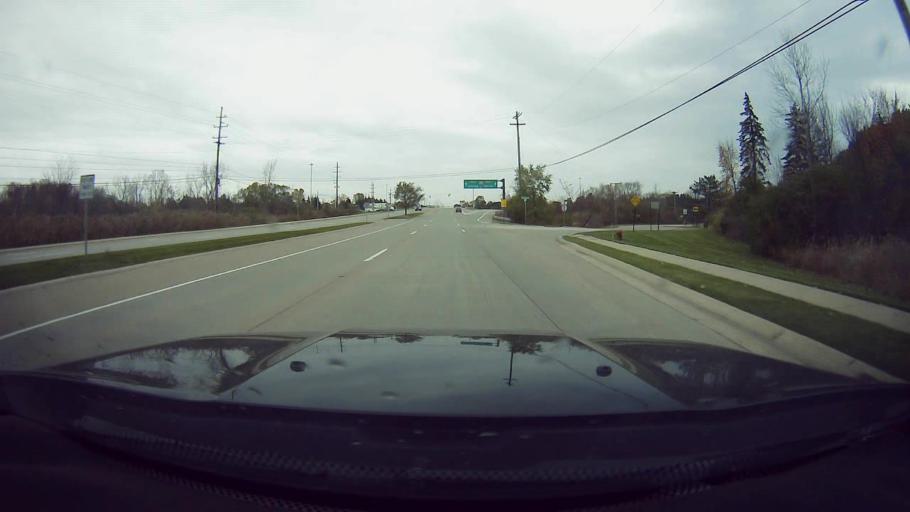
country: US
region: Michigan
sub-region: Oakland County
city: Farmington Hills
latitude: 42.4926
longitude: -83.3581
